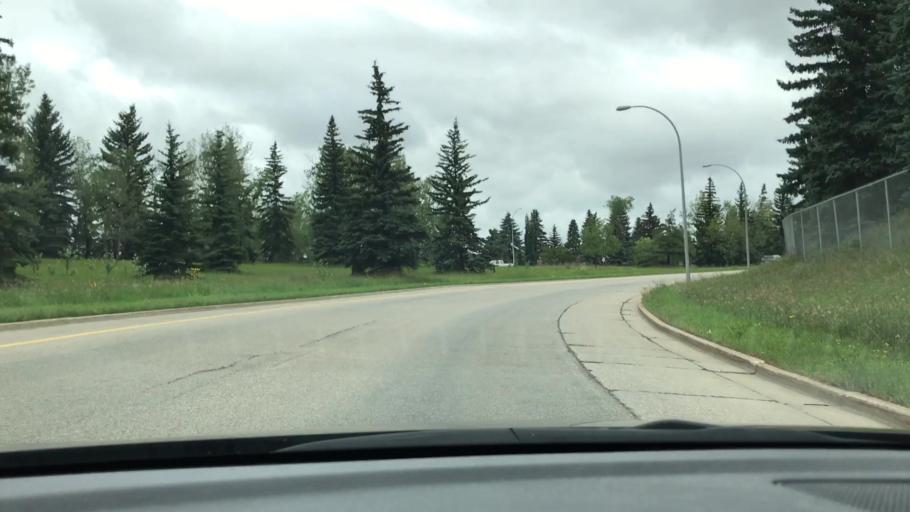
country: CA
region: Alberta
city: Edmonton
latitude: 53.5125
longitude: -113.5781
